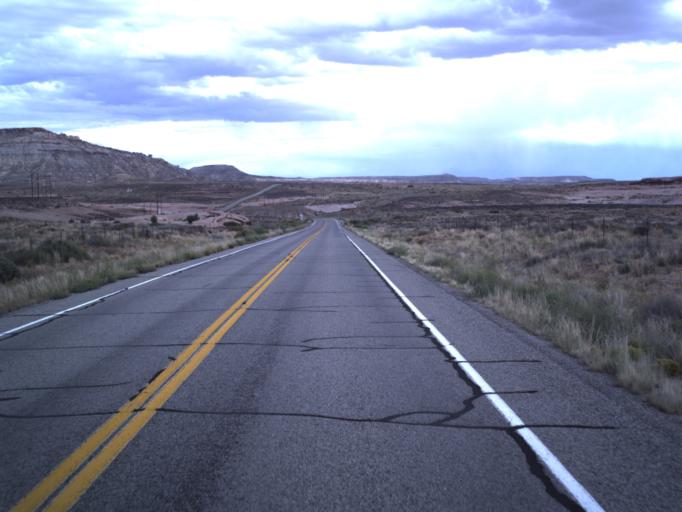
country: US
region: Utah
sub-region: San Juan County
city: Blanding
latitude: 37.2980
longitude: -109.4681
